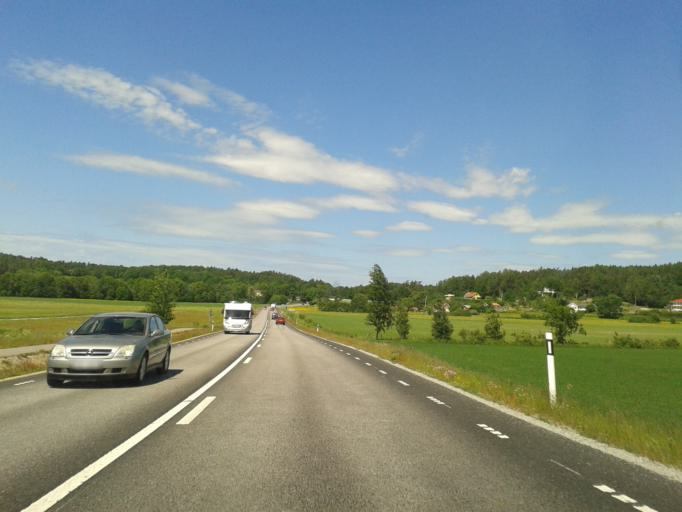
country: SE
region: Vaestra Goetaland
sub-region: Orust
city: Henan
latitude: 58.3110
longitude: 11.6953
